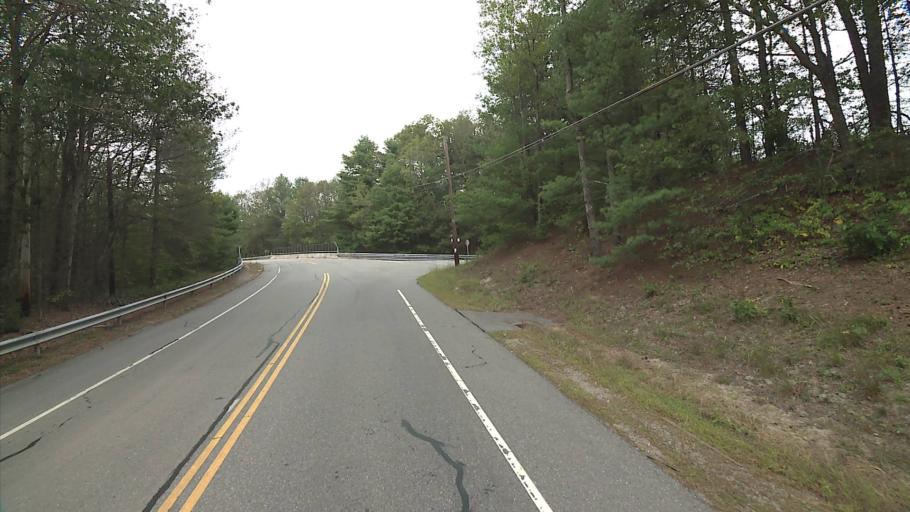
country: US
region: Connecticut
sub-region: New London County
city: Jewett City
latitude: 41.6499
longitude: -71.9636
